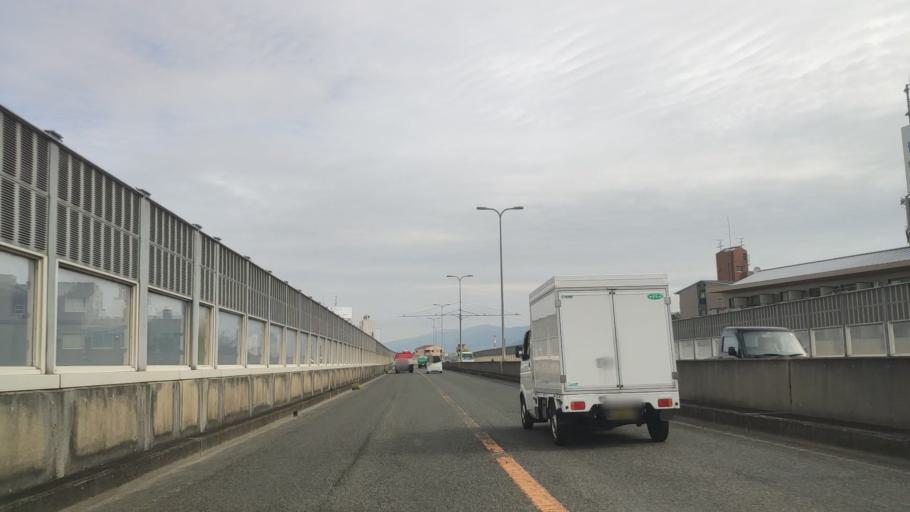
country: JP
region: Osaka
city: Kashihara
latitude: 34.5598
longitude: 135.6002
